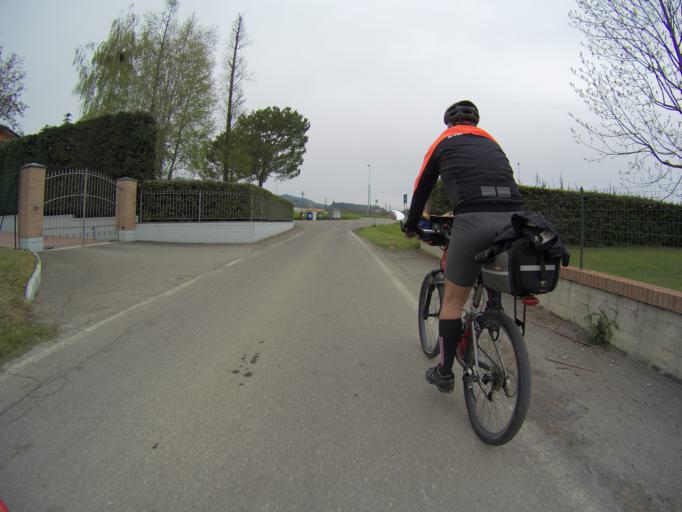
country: IT
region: Emilia-Romagna
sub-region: Provincia di Reggio Emilia
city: San Polo d'Enza
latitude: 44.6346
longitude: 10.4333
